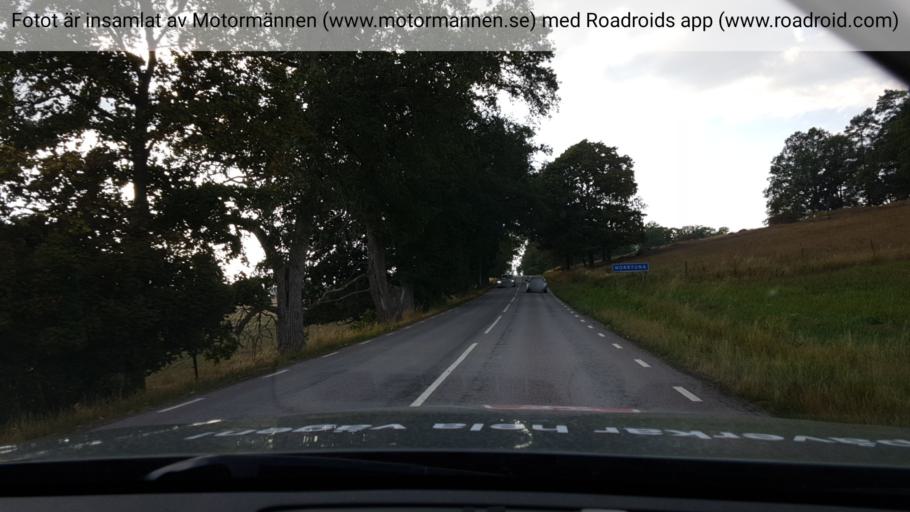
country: SE
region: Soedermanland
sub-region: Gnesta Kommun
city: Gnesta
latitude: 59.0784
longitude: 17.2799
